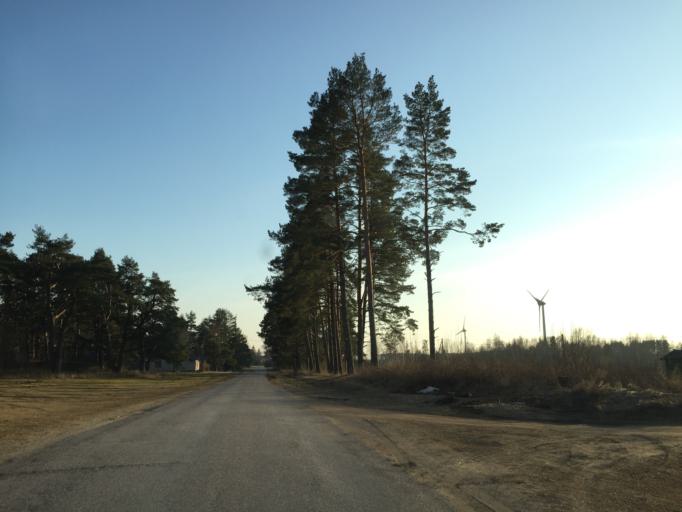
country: EE
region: Laeaene
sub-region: Lihula vald
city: Lihula
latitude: 58.4558
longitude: 23.7486
